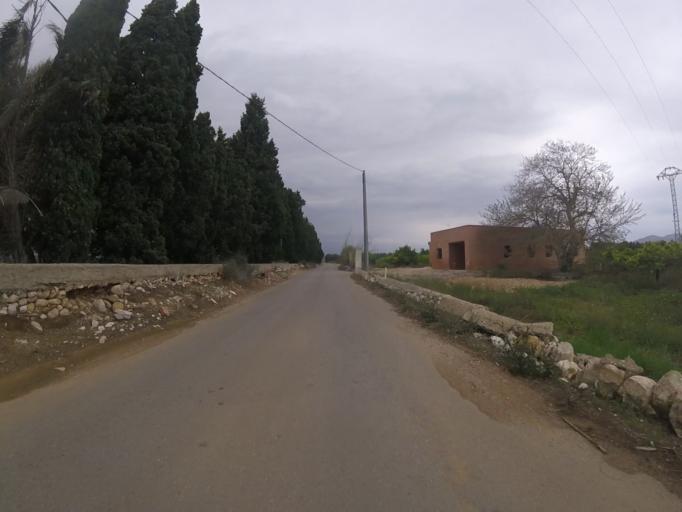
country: ES
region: Valencia
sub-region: Provincia de Castello
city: Alcoceber
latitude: 40.2092
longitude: 0.2529
